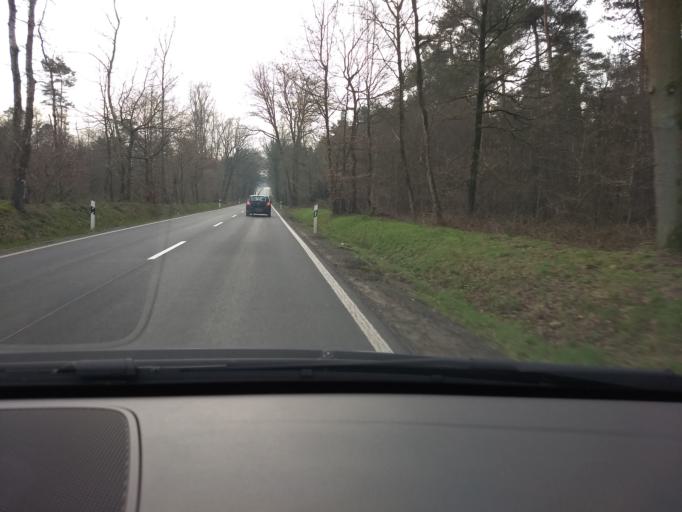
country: DE
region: North Rhine-Westphalia
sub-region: Regierungsbezirk Munster
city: Heiden
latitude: 51.8591
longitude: 6.9192
